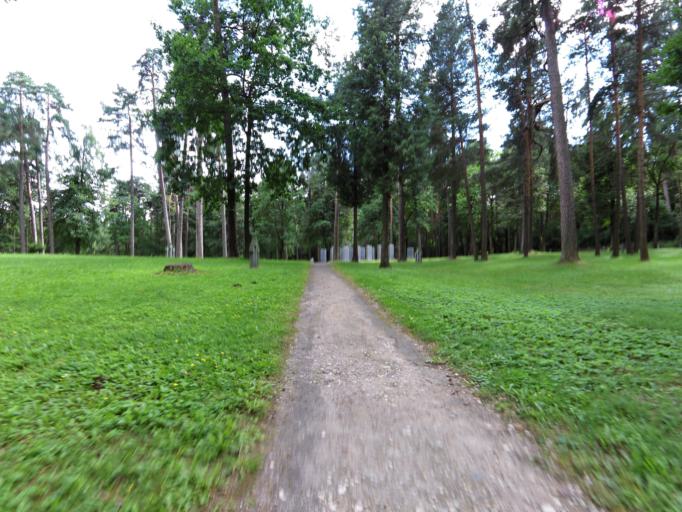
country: LT
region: Vilnius County
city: Vilkpede
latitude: 54.6845
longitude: 25.2462
